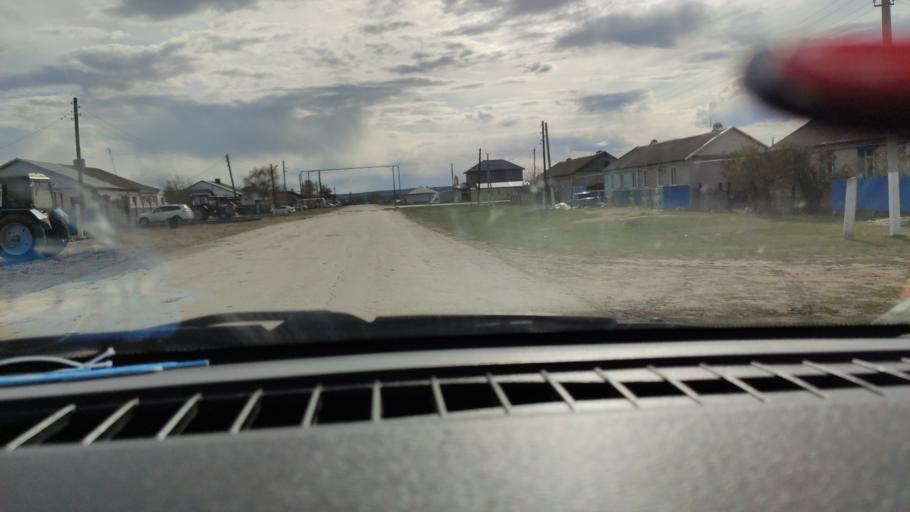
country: RU
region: Saratov
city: Rovnoye
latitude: 50.9299
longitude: 46.0863
